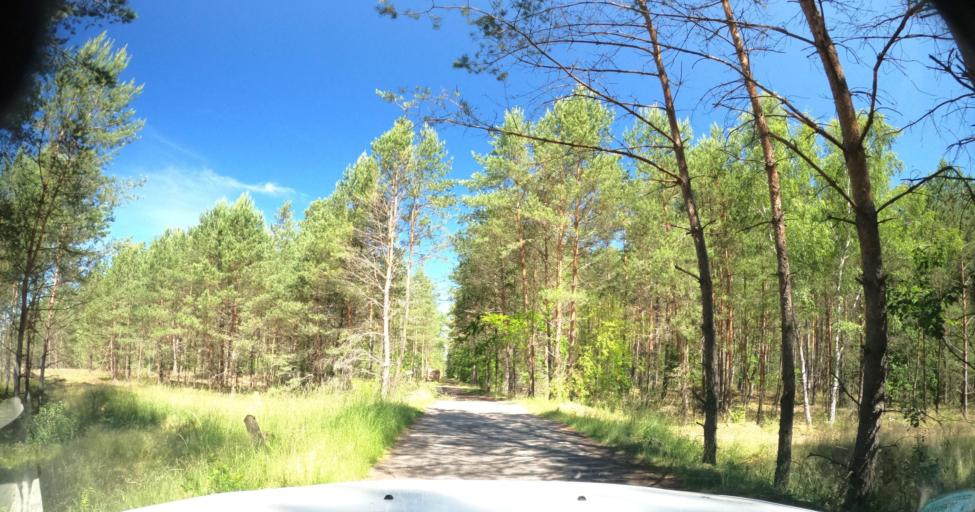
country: PL
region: West Pomeranian Voivodeship
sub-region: Powiat szczecinecki
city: Lubowo
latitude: 53.5877
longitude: 16.4582
